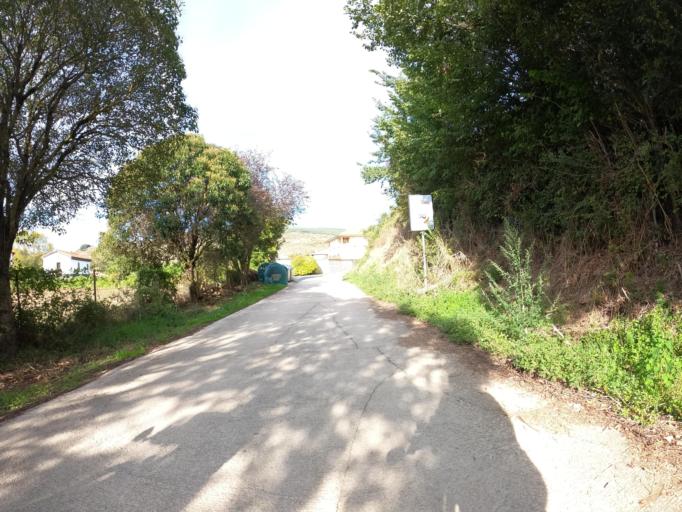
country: ES
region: Navarre
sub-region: Provincia de Navarra
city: Oltza
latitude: 42.8014
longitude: -1.7734
